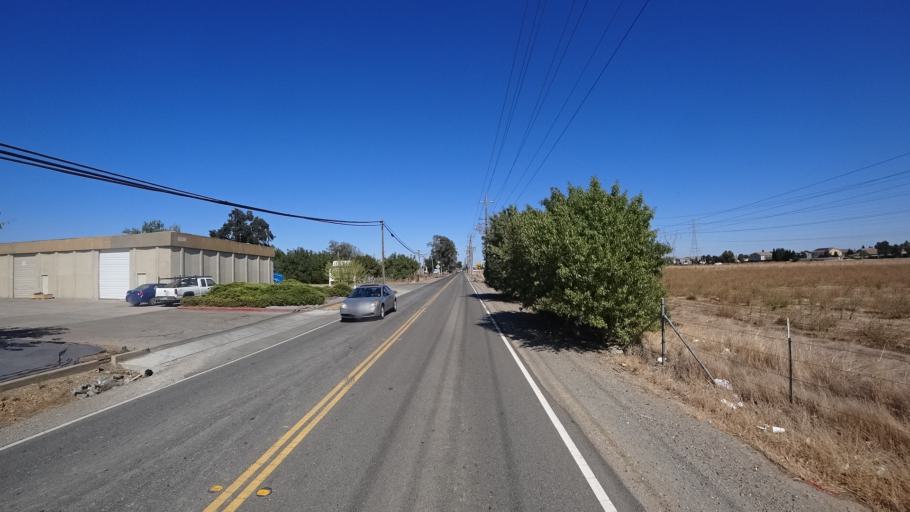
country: US
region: California
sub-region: Sacramento County
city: Elk Grove
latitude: 38.3890
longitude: -121.3529
